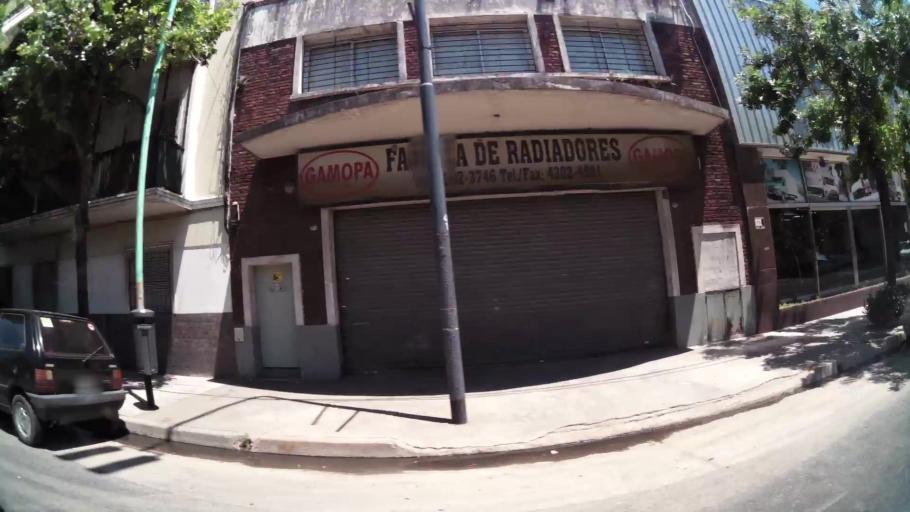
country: AR
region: Buenos Aires
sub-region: Partido de Avellaneda
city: Avellaneda
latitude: -34.6534
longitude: -58.3890
